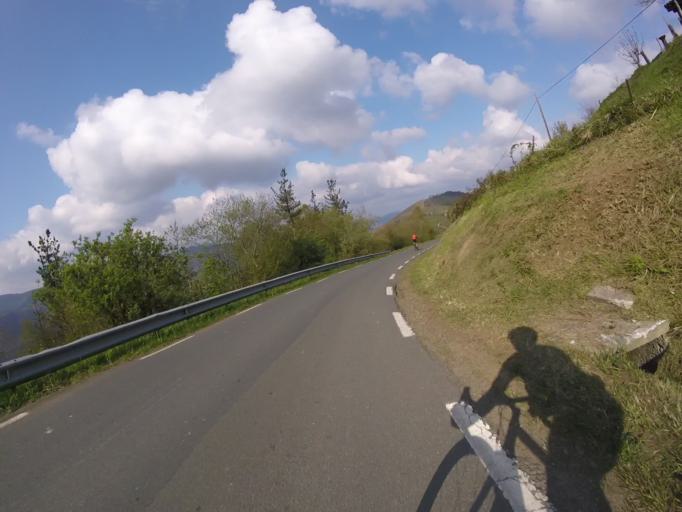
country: ES
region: Basque Country
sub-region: Provincia de Guipuzcoa
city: Azkoitia
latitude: 43.2064
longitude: -2.3368
